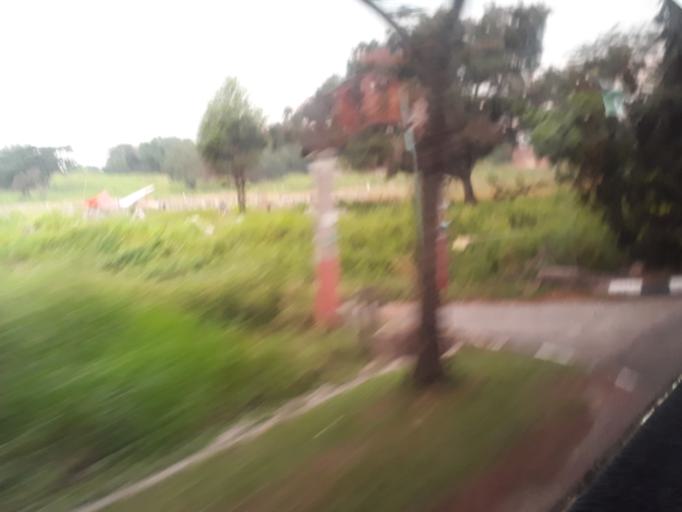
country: MY
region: Perak
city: Ipoh
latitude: 4.6007
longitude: 101.1141
